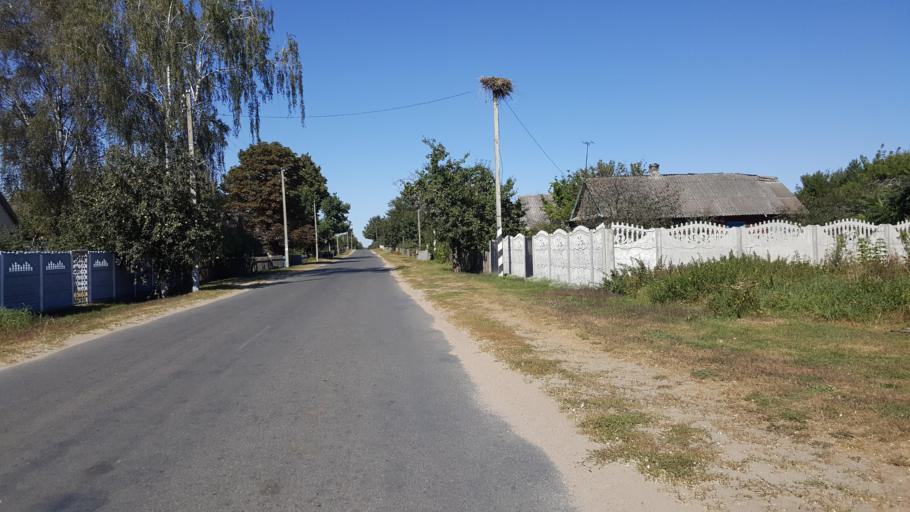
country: PL
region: Lublin Voivodeship
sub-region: Powiat bialski
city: Rokitno
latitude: 52.2346
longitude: 23.3414
